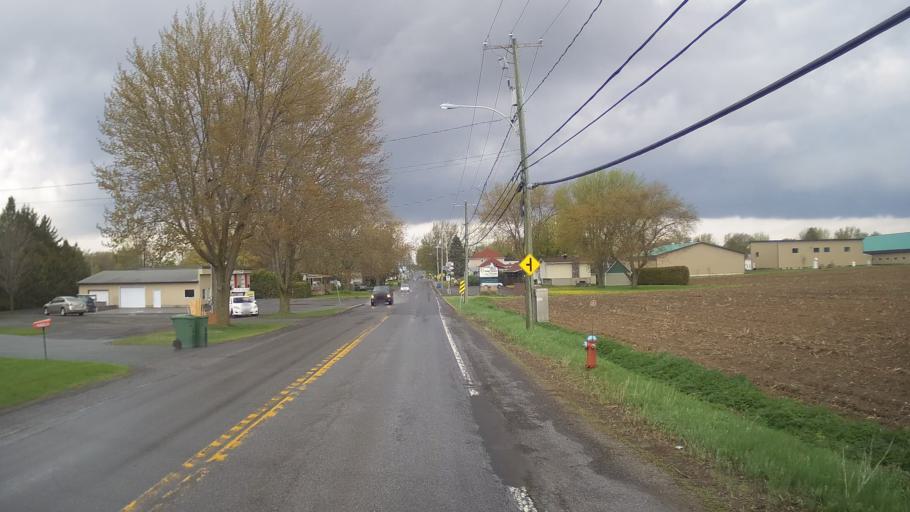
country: CA
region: Quebec
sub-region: Monteregie
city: Farnham
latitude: 45.3198
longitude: -73.0600
